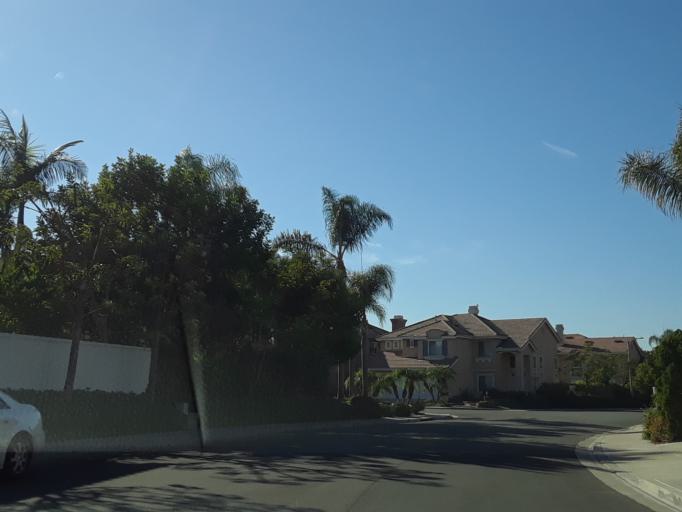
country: US
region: California
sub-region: Orange County
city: Irvine
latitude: 33.6916
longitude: -117.8021
